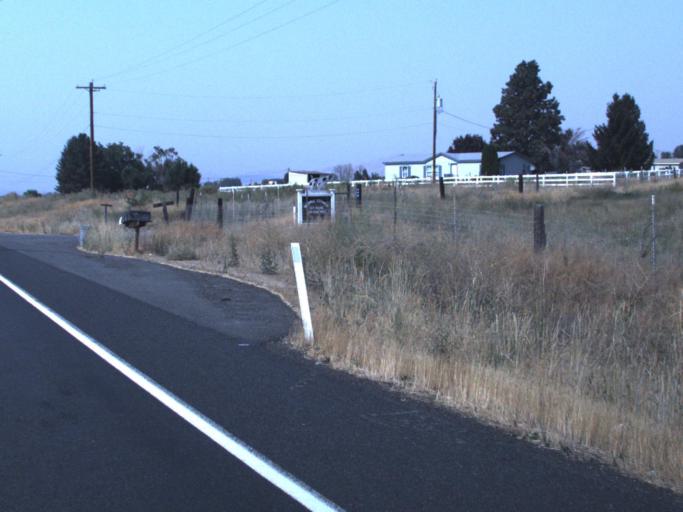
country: US
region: Washington
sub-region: Yakima County
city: Zillah
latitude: 46.5360
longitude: -120.2954
